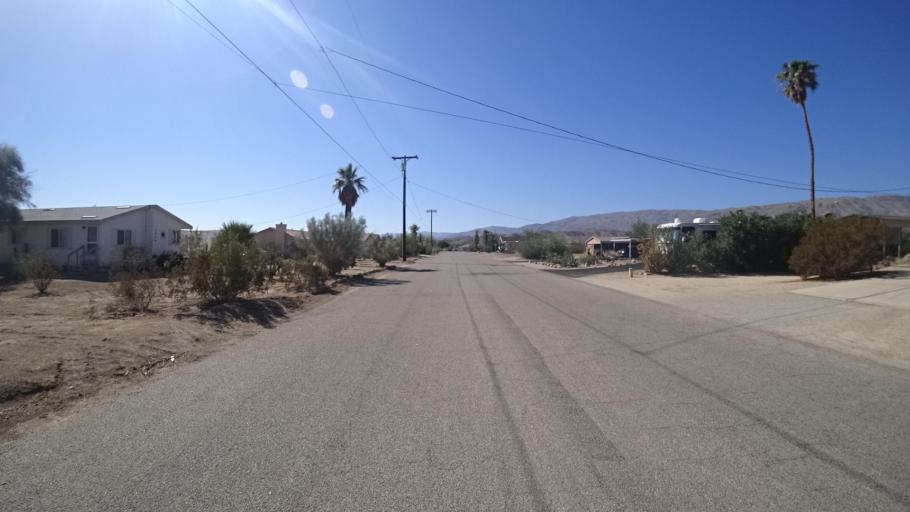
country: US
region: California
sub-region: San Diego County
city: Borrego Springs
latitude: 33.2721
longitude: -116.3909
